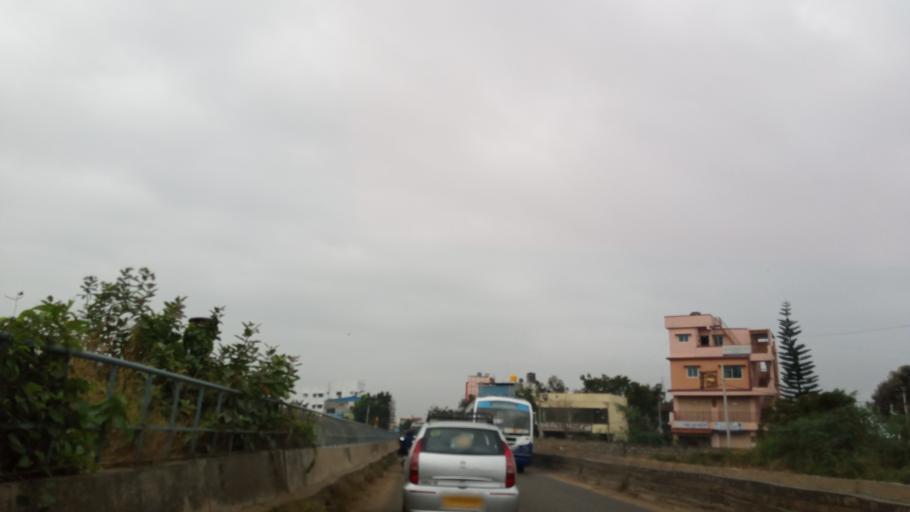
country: IN
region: Karnataka
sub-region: Bangalore Urban
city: Bangalore
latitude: 12.9041
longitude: 77.5258
